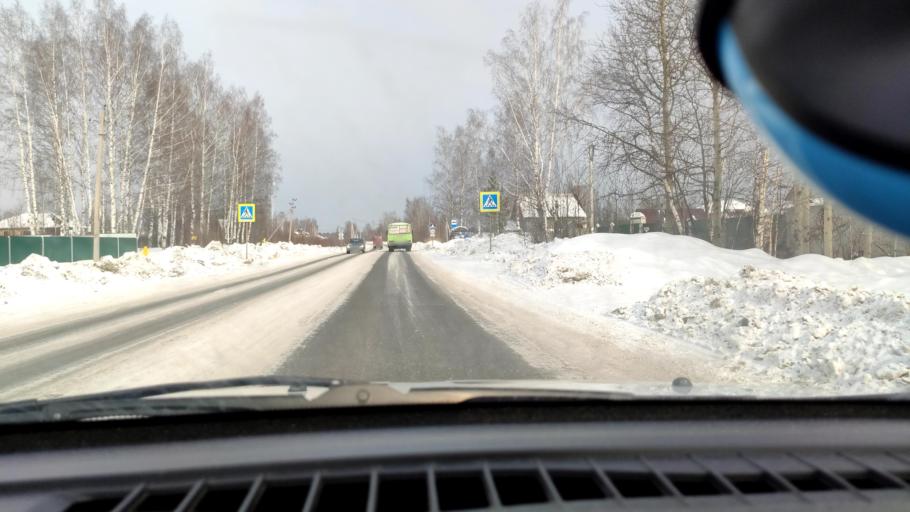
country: RU
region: Perm
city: Krasnokamsk
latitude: 58.0913
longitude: 55.8027
